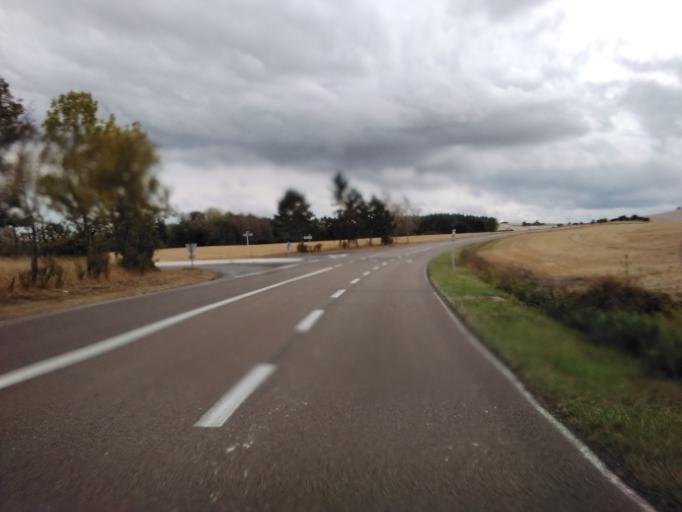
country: FR
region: Champagne-Ardenne
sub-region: Departement de la Marne
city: Frignicourt
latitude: 48.6671
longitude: 4.5840
